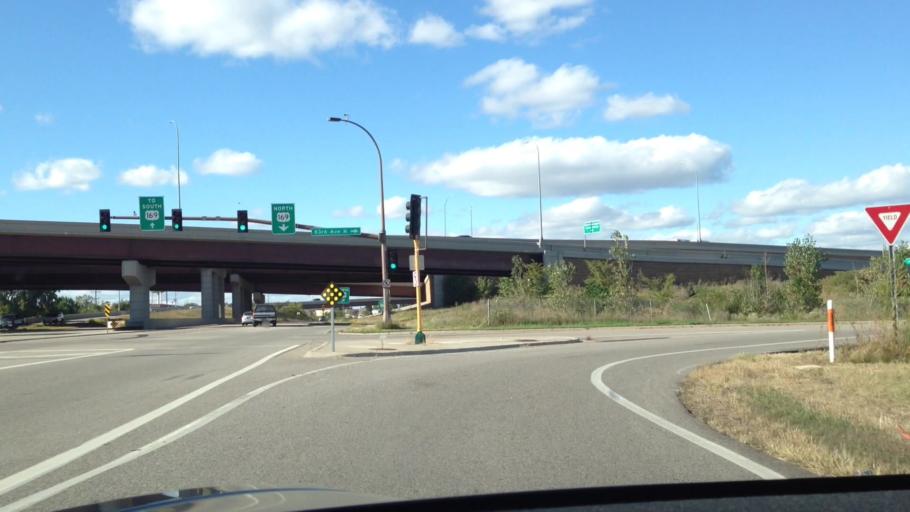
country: US
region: Minnesota
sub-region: Hennepin County
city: Osseo
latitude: 45.1049
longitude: -93.3921
